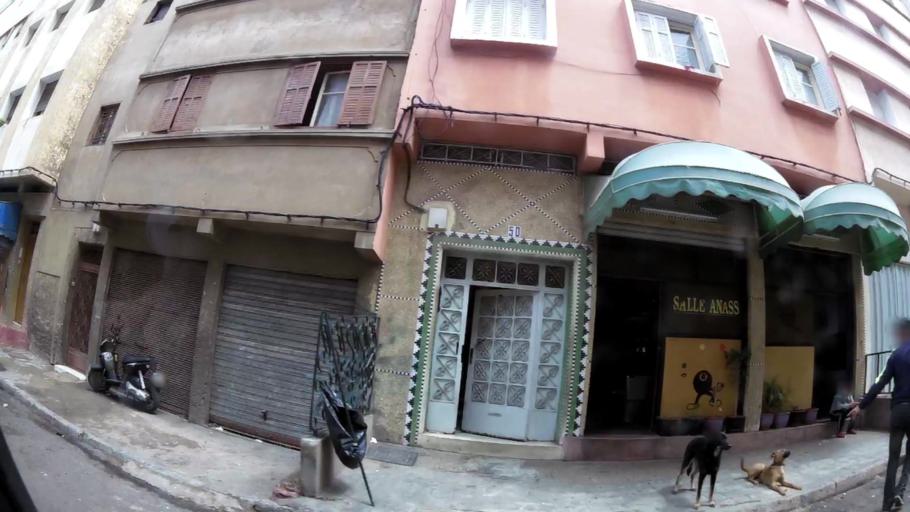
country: MA
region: Grand Casablanca
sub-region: Mediouna
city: Tit Mellil
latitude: 33.6059
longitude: -7.5142
